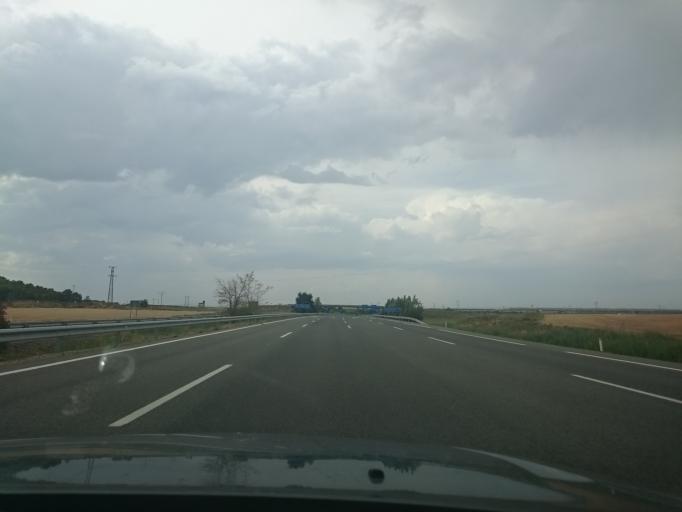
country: ES
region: Navarre
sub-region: Provincia de Navarra
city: Corella
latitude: 42.0878
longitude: -1.7156
